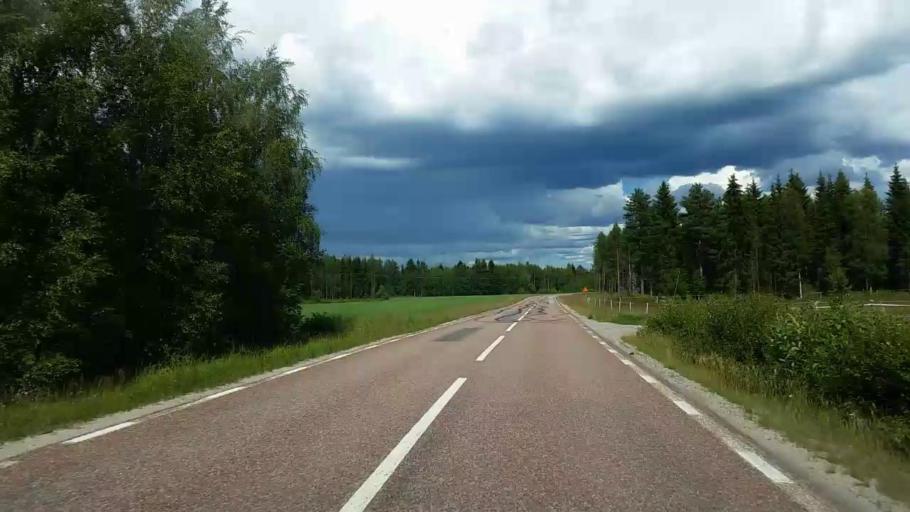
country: SE
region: Gaevleborg
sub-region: Ovanakers Kommun
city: Edsbyn
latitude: 61.3389
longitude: 15.5425
